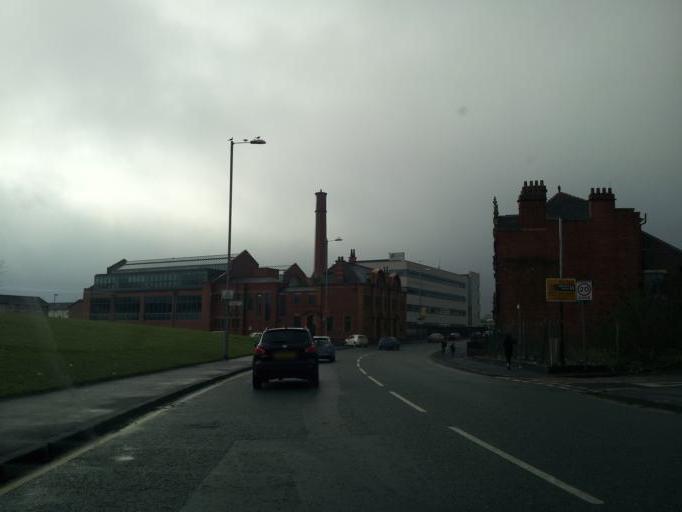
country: GB
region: England
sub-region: Manchester
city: Blackley
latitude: 53.5156
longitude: -2.2126
